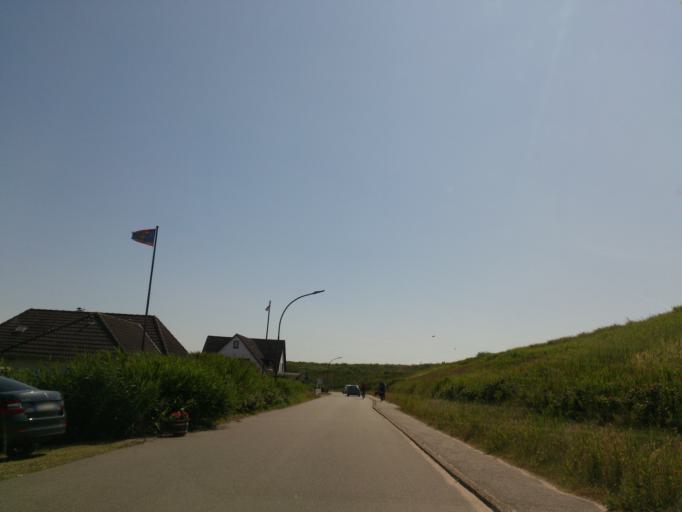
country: DE
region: Schleswig-Holstein
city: Sankt Peter-Ording
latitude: 54.3399
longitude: 8.6025
